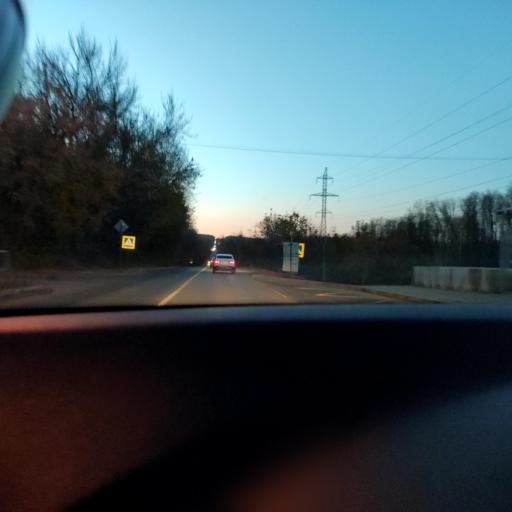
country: RU
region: Samara
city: Petra-Dubrava
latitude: 53.3080
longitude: 50.2779
